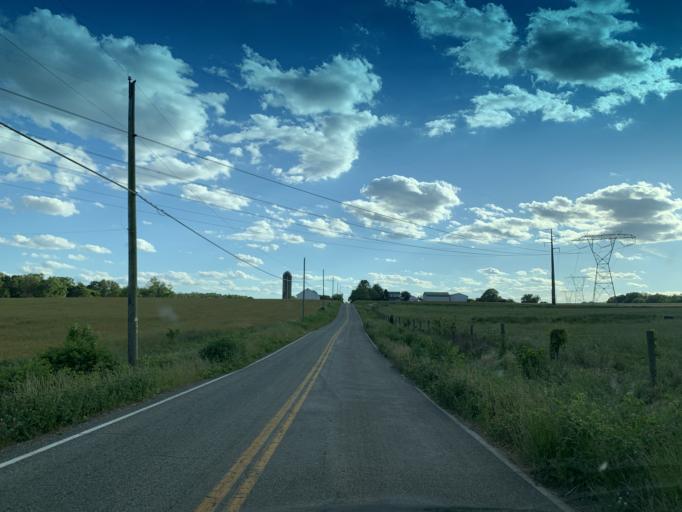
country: US
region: Maryland
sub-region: Cecil County
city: Rising Sun
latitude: 39.6714
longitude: -75.9980
